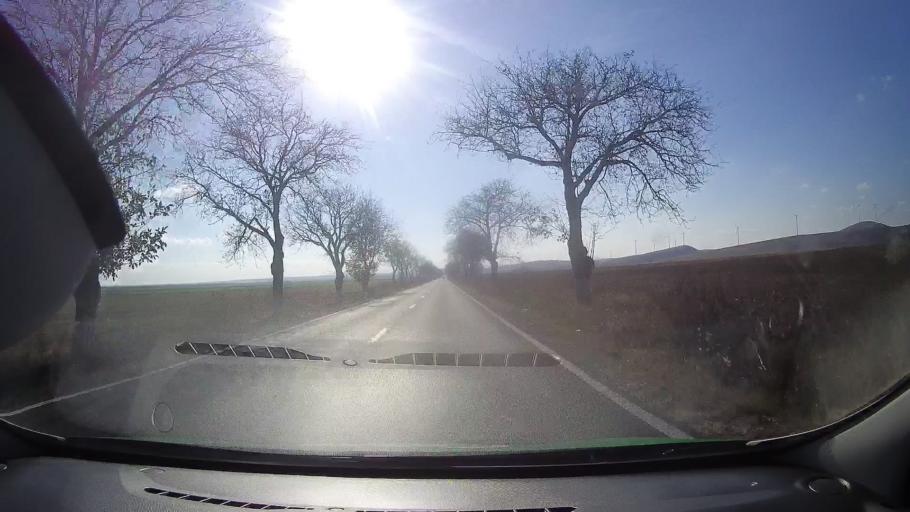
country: RO
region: Tulcea
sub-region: Comuna Ceamurlia de Jos
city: Ceamurlia de Jos
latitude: 44.7975
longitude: 28.6903
